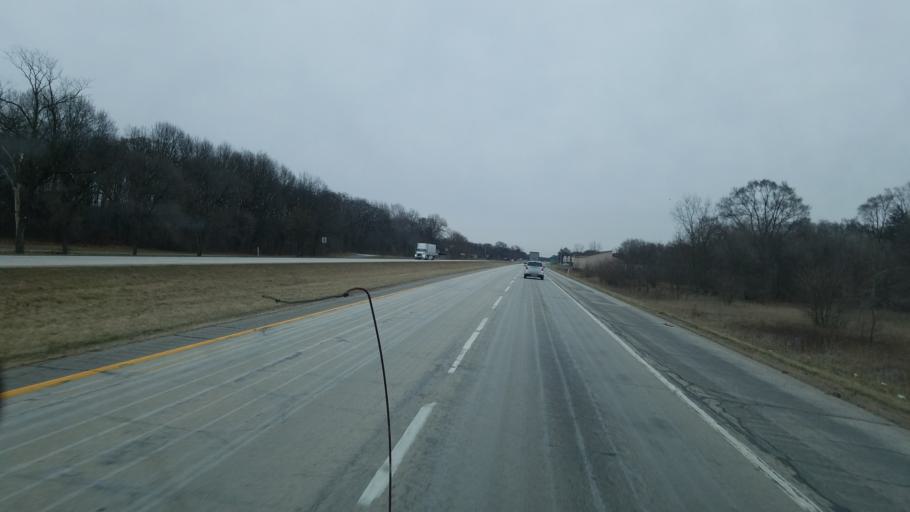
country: US
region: Indiana
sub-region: Starke County
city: Koontz Lake
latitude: 41.3724
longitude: -86.5135
